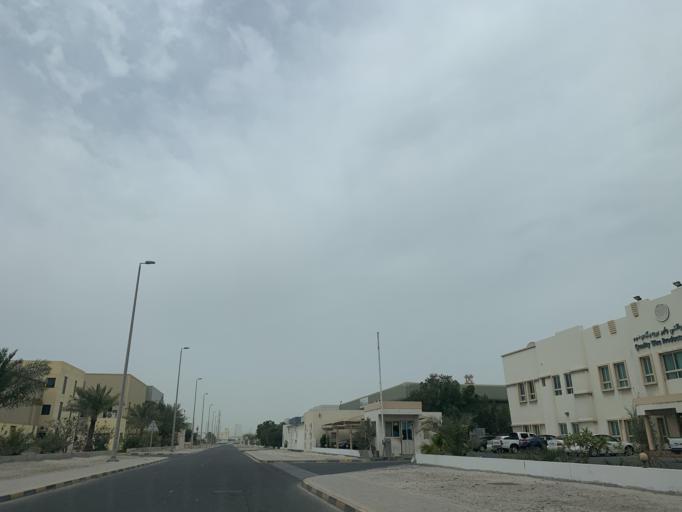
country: BH
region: Muharraq
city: Al Hadd
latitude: 26.2146
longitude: 50.6642
